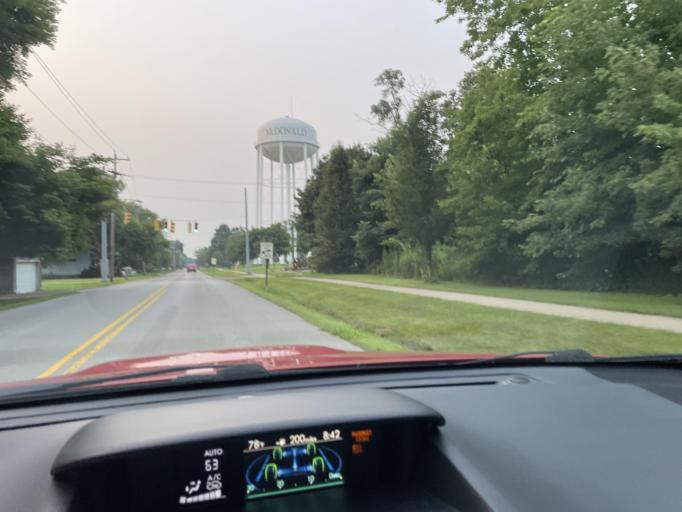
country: US
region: Ohio
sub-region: Trumbull County
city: McDonald
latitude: 41.1597
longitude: -80.7328
